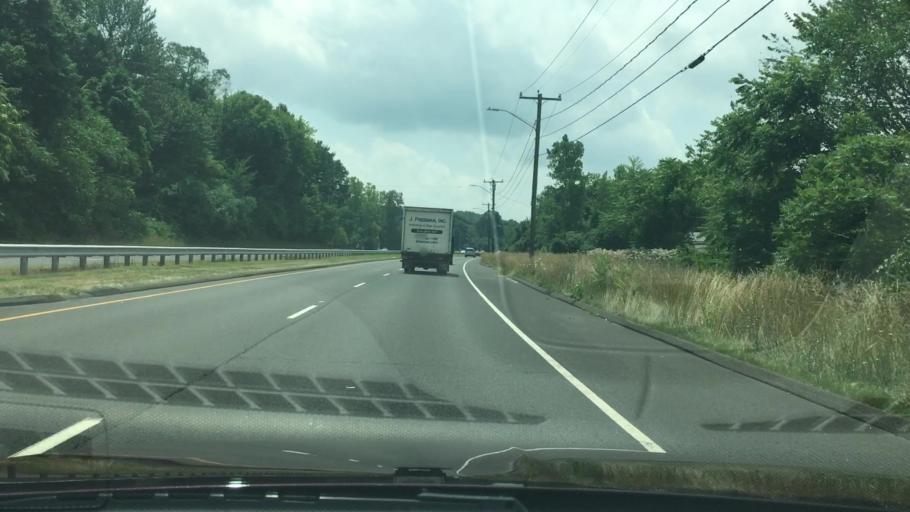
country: US
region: Connecticut
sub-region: Hartford County
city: Kensington
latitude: 41.6196
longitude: -72.7423
